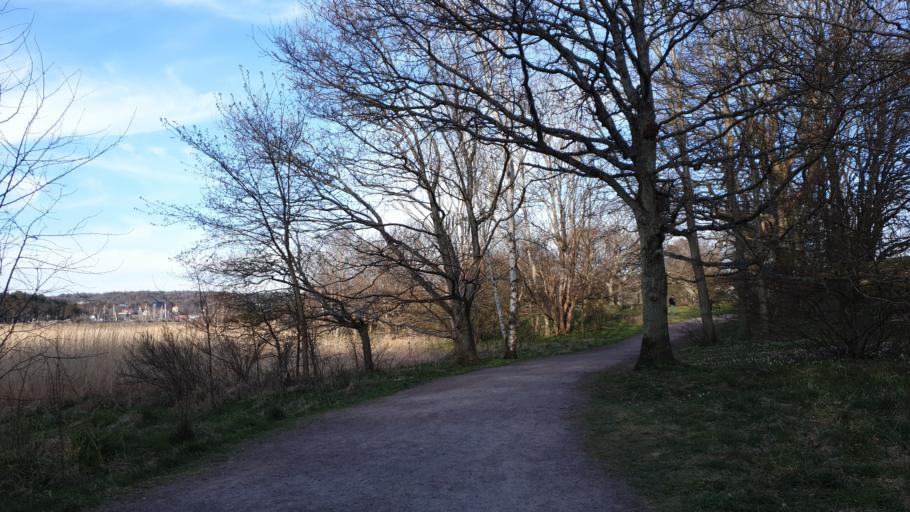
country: SE
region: Vaestra Goetaland
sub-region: Goteborg
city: Billdal
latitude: 57.5939
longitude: 11.9135
